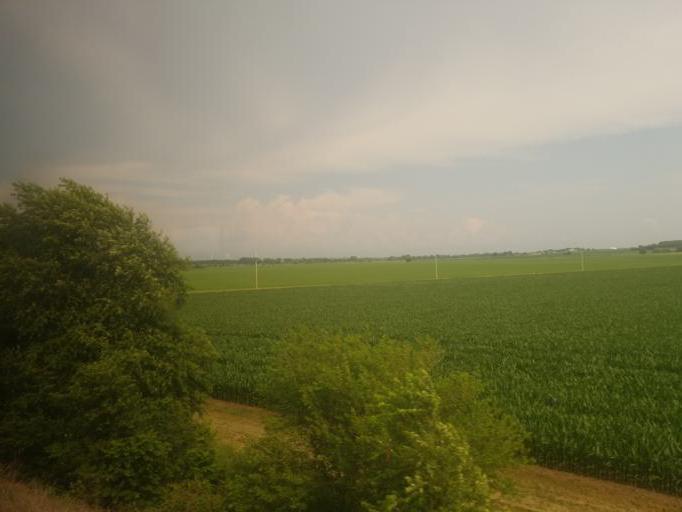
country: US
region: Illinois
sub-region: Henry County
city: Kewanee
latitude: 41.3120
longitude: -89.7051
